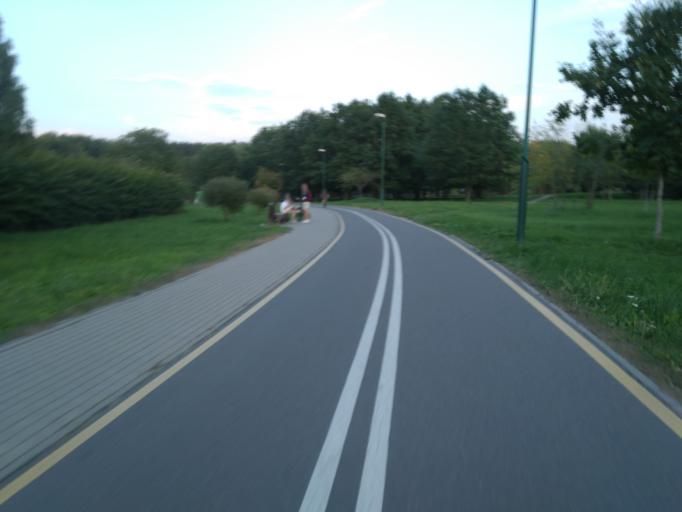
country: BY
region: Minsk
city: Minsk
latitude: 53.9373
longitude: 27.5095
